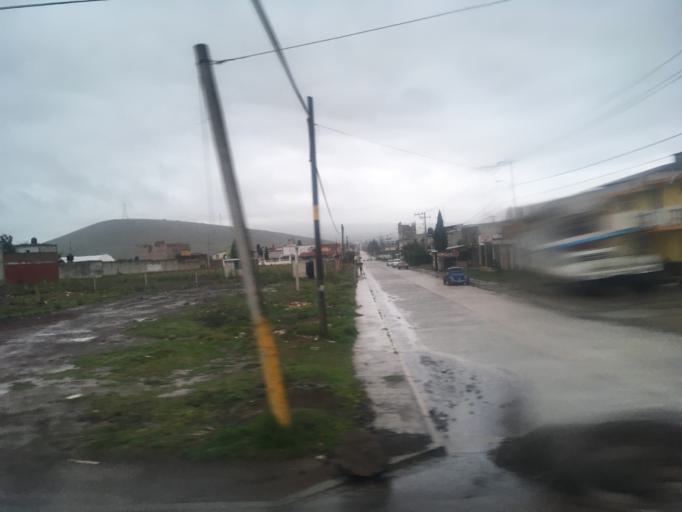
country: MX
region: Puebla
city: Chignahuapan
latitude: 19.8453
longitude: -98.0294
